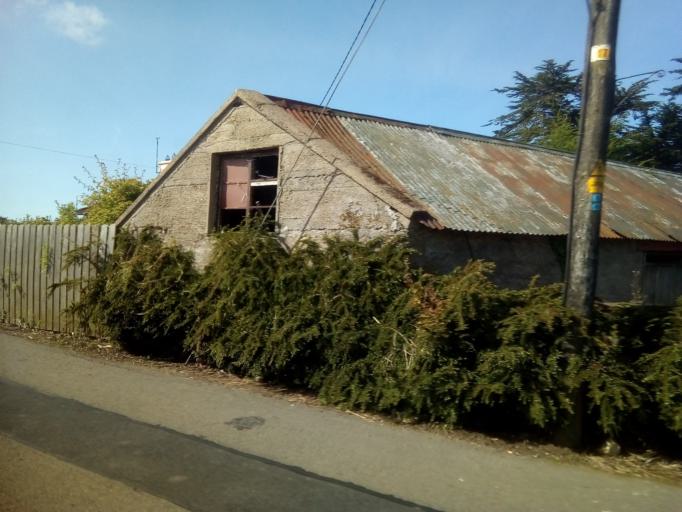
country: IE
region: Leinster
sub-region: Loch Garman
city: Loch Garman
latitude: 52.2284
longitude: -6.5503
